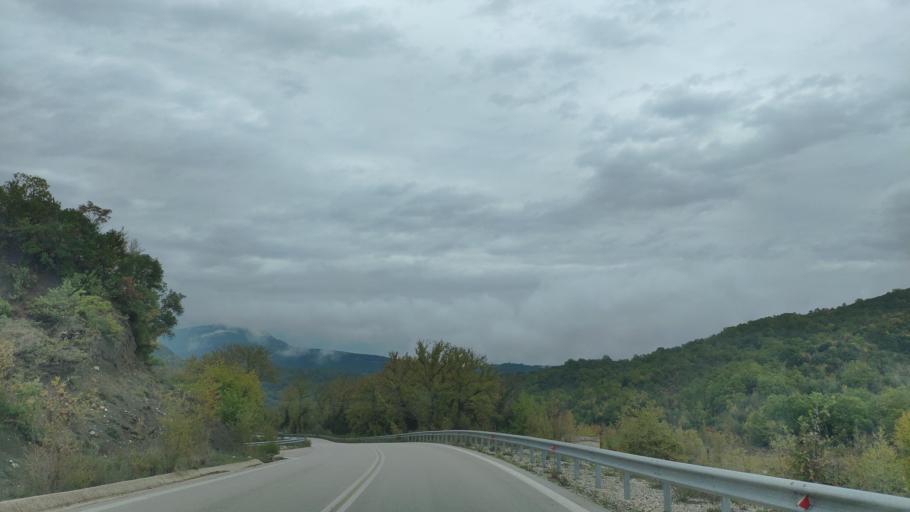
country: GR
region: Epirus
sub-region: Nomos Ioanninon
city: Pedini
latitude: 39.5264
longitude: 20.6936
